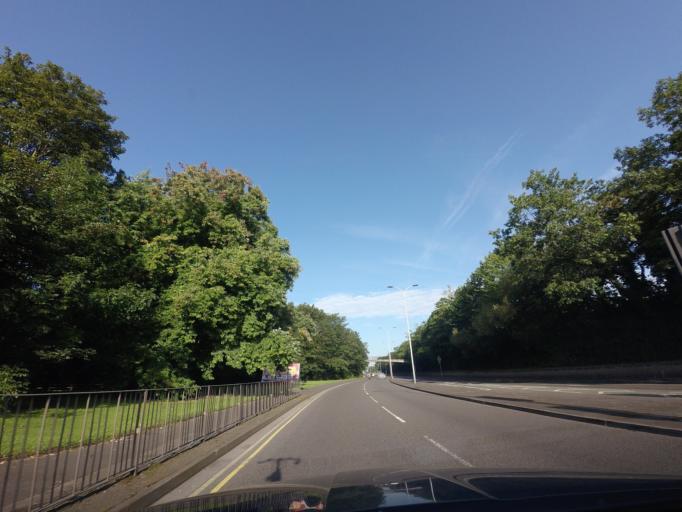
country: GB
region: England
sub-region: Derbyshire
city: Chesterfield
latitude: 53.2337
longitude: -1.4313
